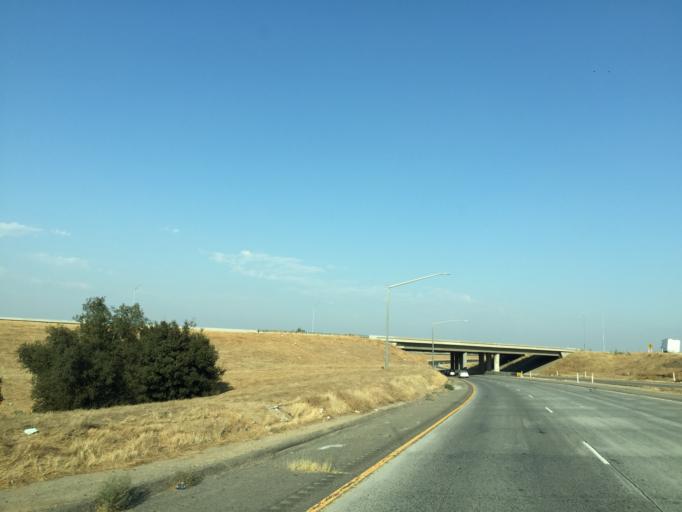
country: US
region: California
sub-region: Tulare County
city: Goshen
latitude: 36.3266
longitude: -119.4089
